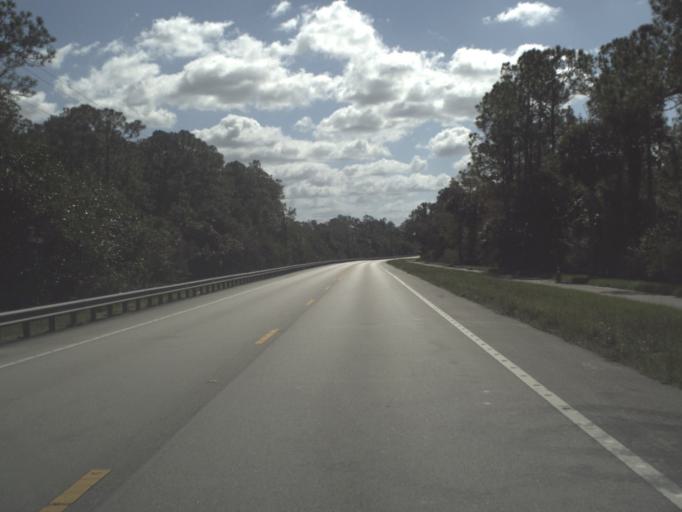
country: US
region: Florida
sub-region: Collier County
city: Lely Resort
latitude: 25.9974
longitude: -81.5965
